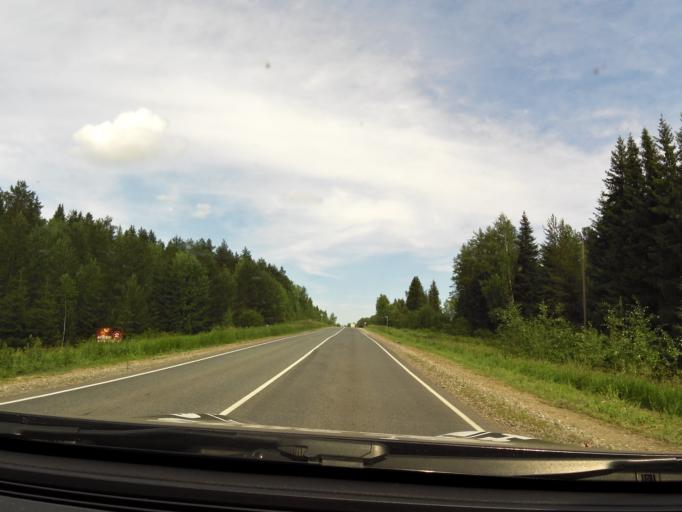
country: RU
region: Kirov
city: Slobodskoy
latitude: 58.7317
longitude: 50.2746
